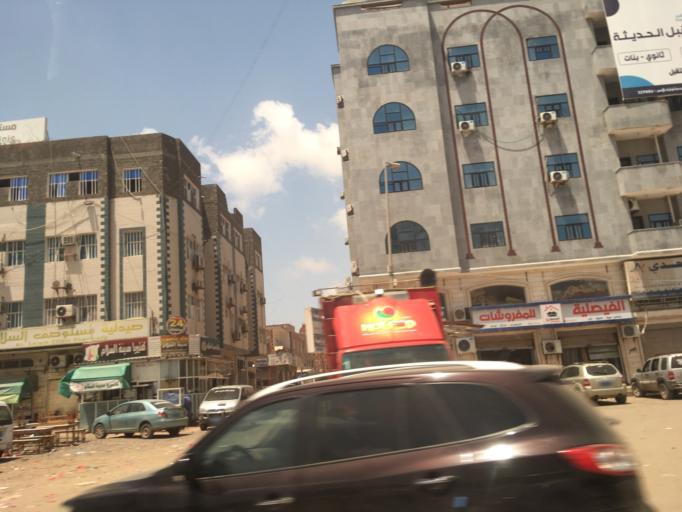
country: YE
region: Aden
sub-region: Al Mansura
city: Al Mansurah
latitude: 12.8597
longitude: 44.9723
